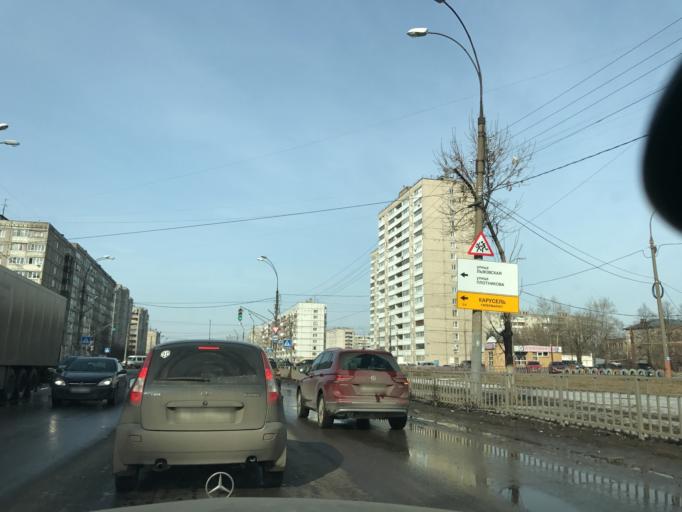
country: RU
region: Nizjnij Novgorod
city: Nizhniy Novgorod
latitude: 56.2701
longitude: 43.8876
